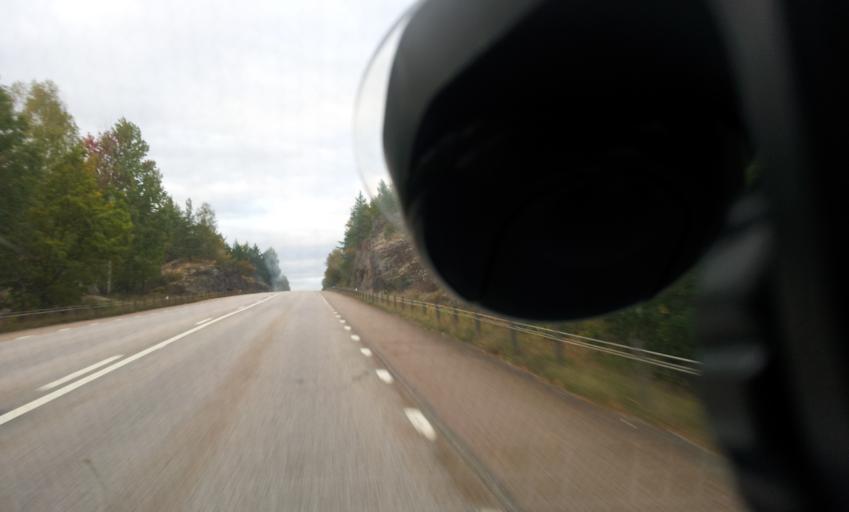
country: SE
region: Kalmar
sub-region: Oskarshamns Kommun
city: Oskarshamn
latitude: 57.5041
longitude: 16.5030
